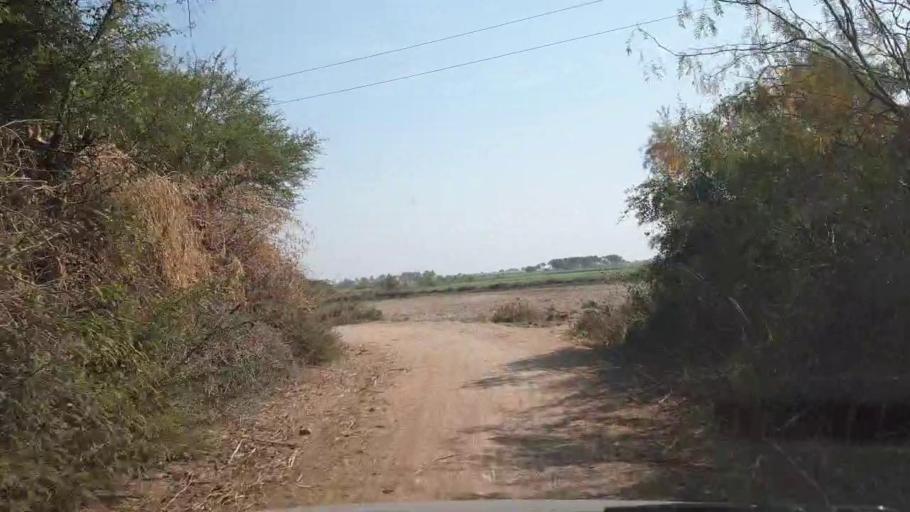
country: PK
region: Sindh
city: Chambar
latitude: 25.3499
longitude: 68.8243
